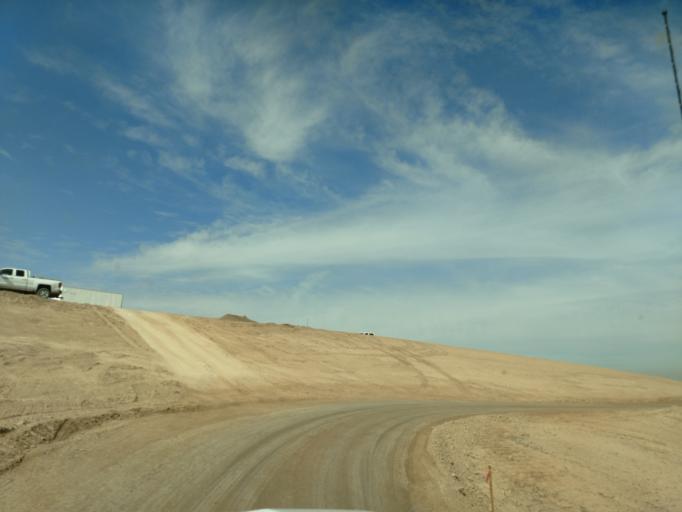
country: US
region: Arizona
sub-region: Maricopa County
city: Laveen
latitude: 33.3488
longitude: -112.1883
